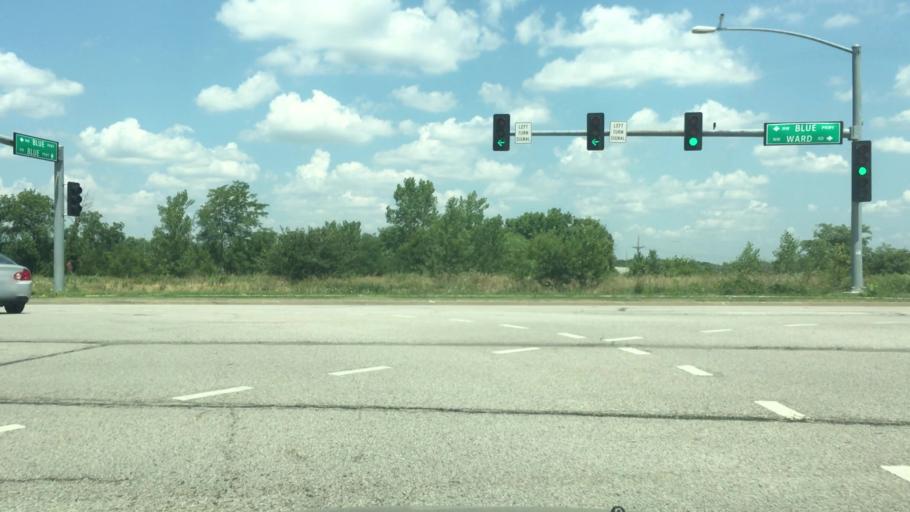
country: US
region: Missouri
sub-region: Jackson County
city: Lees Summit
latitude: 38.9332
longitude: -94.4006
